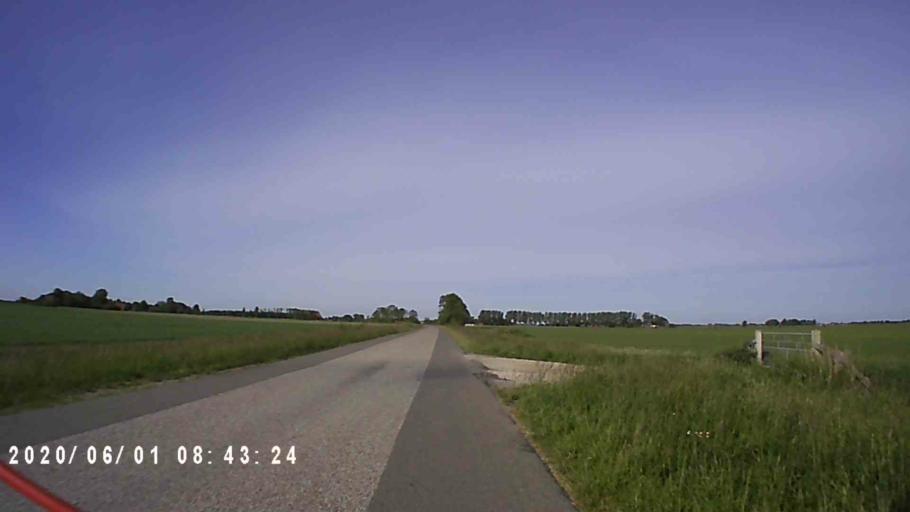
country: NL
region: Friesland
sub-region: Gemeente Ferwerderadiel
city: Burdaard
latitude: 53.2834
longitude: 5.8424
